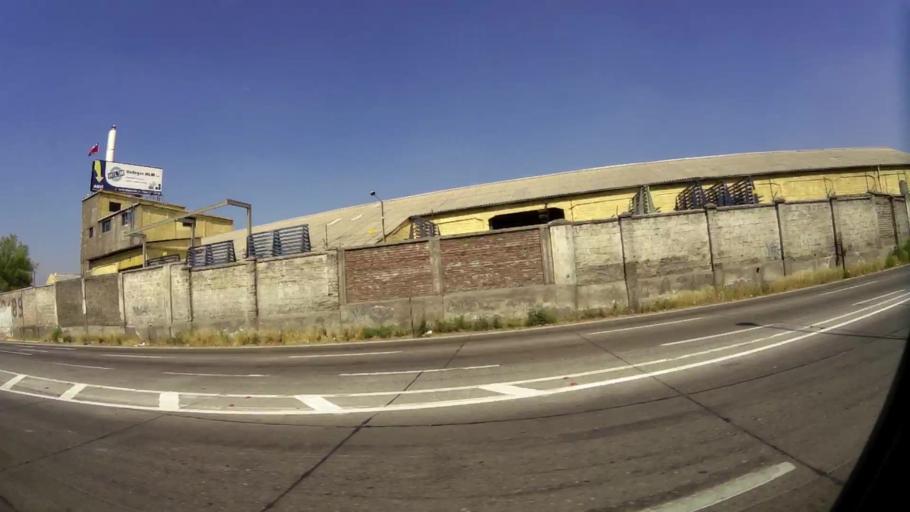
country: CL
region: Santiago Metropolitan
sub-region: Provincia de Santiago
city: Santiago
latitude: -33.4765
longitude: -70.6660
